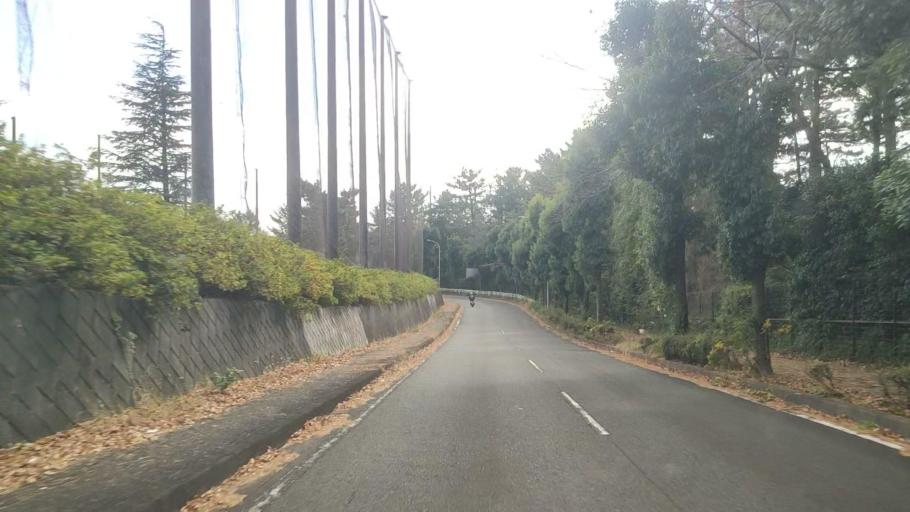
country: JP
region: Kanagawa
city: Yokohama
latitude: 35.4439
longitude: 139.5520
